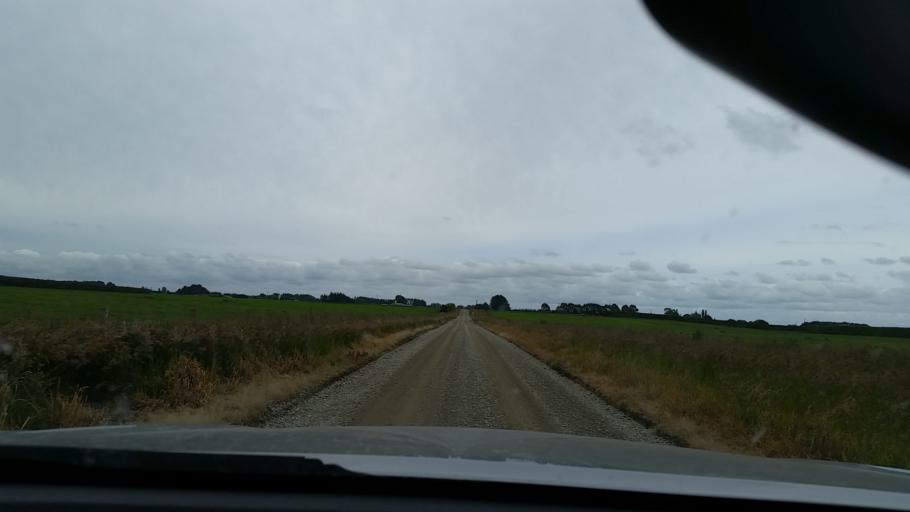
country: NZ
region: Southland
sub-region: Southland District
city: Winton
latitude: -46.2471
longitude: 168.3222
